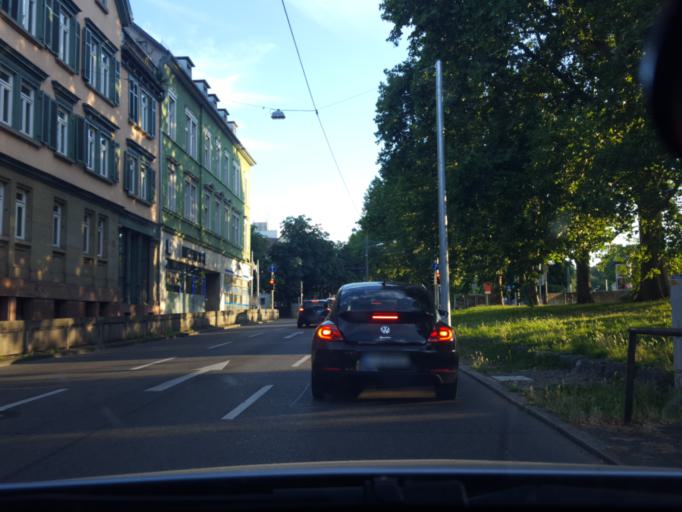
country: DE
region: Baden-Wuerttemberg
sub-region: Regierungsbezirk Stuttgart
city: Stuttgart-Ost
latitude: 48.8063
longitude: 9.2137
